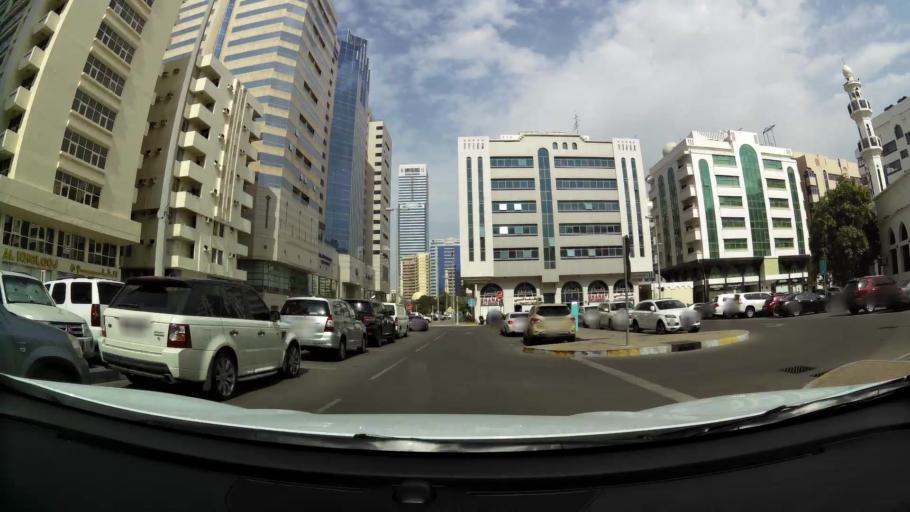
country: AE
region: Abu Dhabi
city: Abu Dhabi
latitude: 24.4794
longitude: 54.3567
